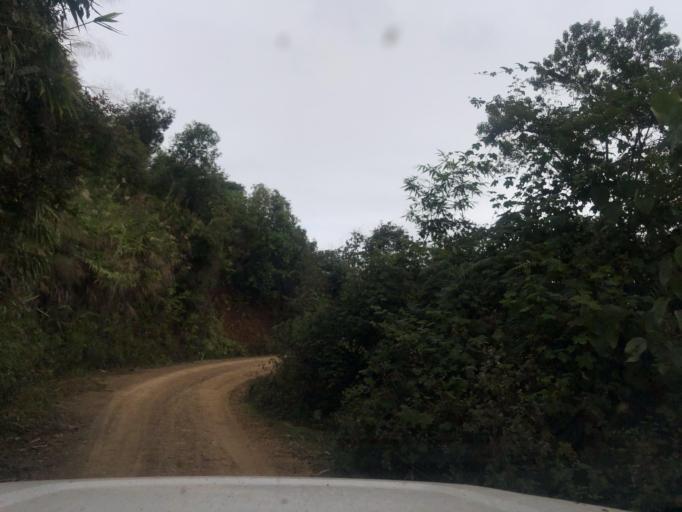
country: LA
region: Phongsali
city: Khoa
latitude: 21.2638
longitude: 102.5892
